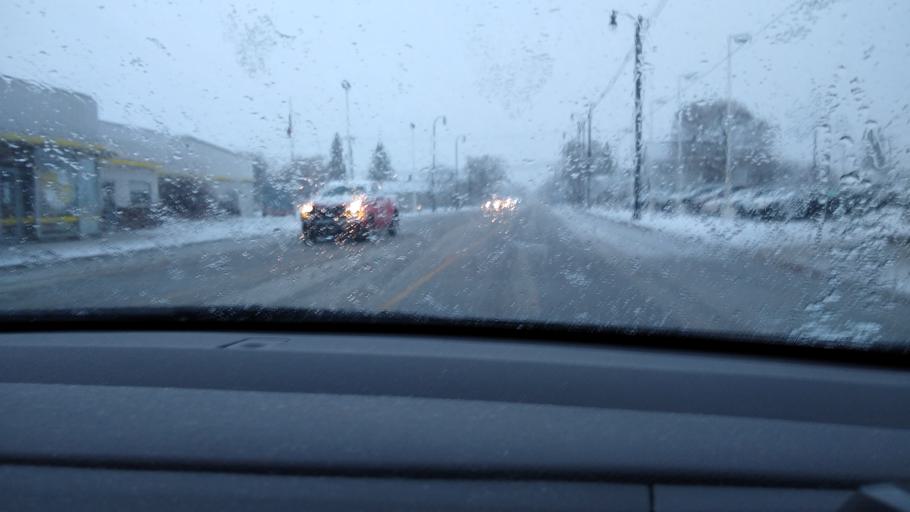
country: US
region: Michigan
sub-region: Delta County
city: Escanaba
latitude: 45.7515
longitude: -87.0717
